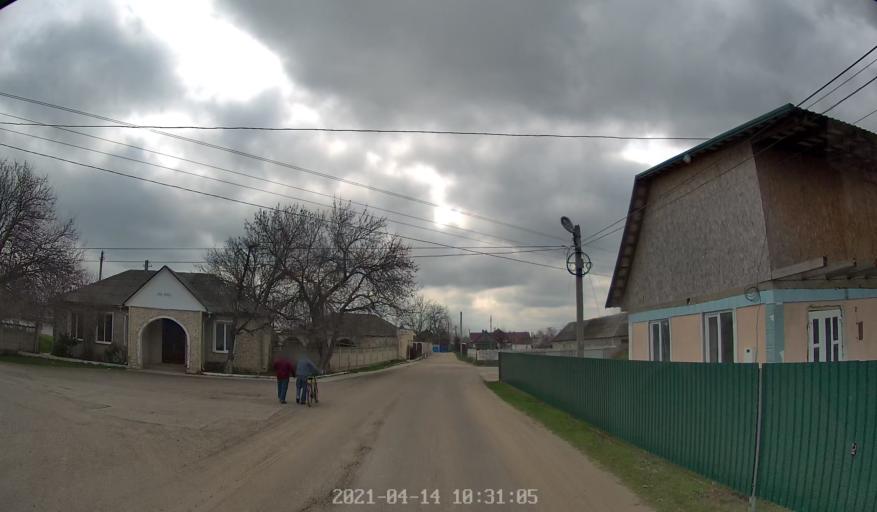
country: MD
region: Criuleni
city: Criuleni
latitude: 47.1466
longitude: 29.1367
